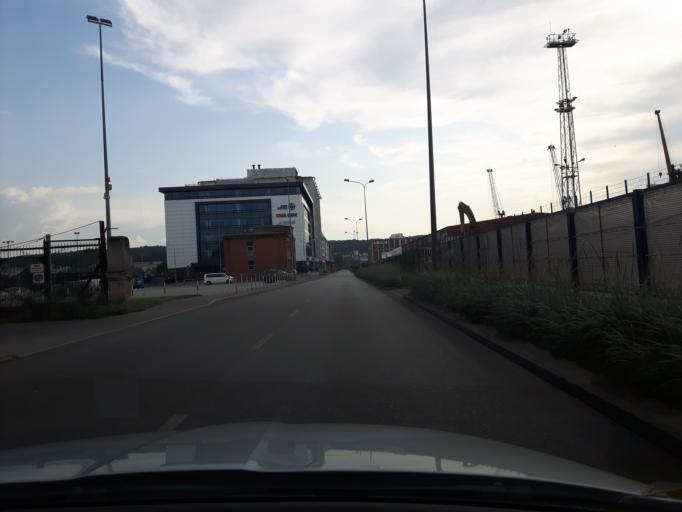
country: PL
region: Pomeranian Voivodeship
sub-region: Gdynia
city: Gdynia
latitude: 54.5305
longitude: 18.5388
